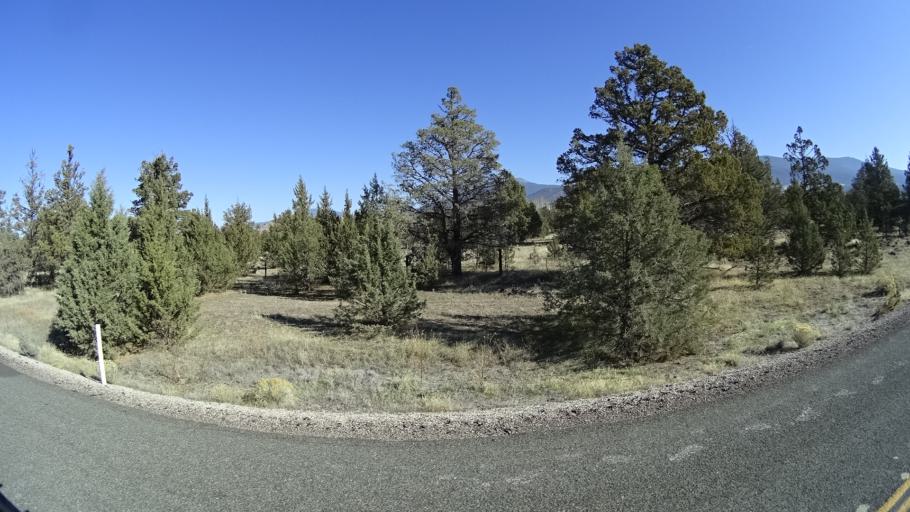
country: US
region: California
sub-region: Siskiyou County
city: Montague
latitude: 41.6468
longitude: -122.3591
